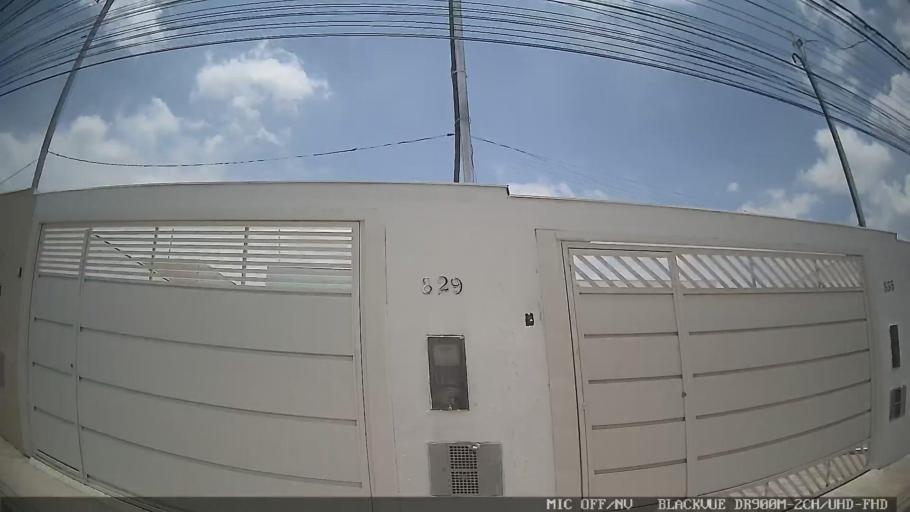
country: BR
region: Sao Paulo
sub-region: Ferraz De Vasconcelos
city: Ferraz de Vasconcelos
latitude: -23.5597
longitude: -46.3757
